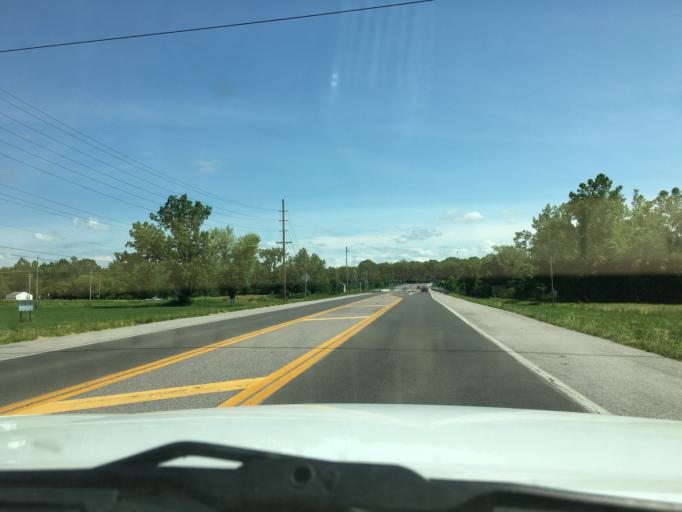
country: US
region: Missouri
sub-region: Franklin County
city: Union
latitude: 38.4495
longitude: -90.9999
